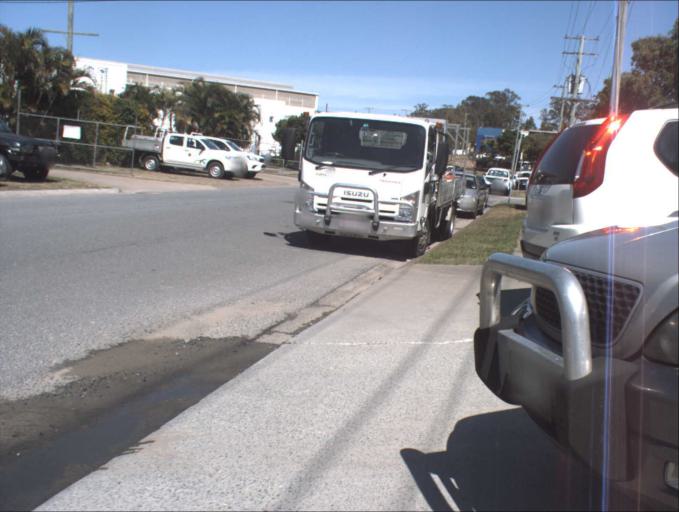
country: AU
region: Queensland
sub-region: Logan
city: Logan City
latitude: -27.6652
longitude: 153.1164
